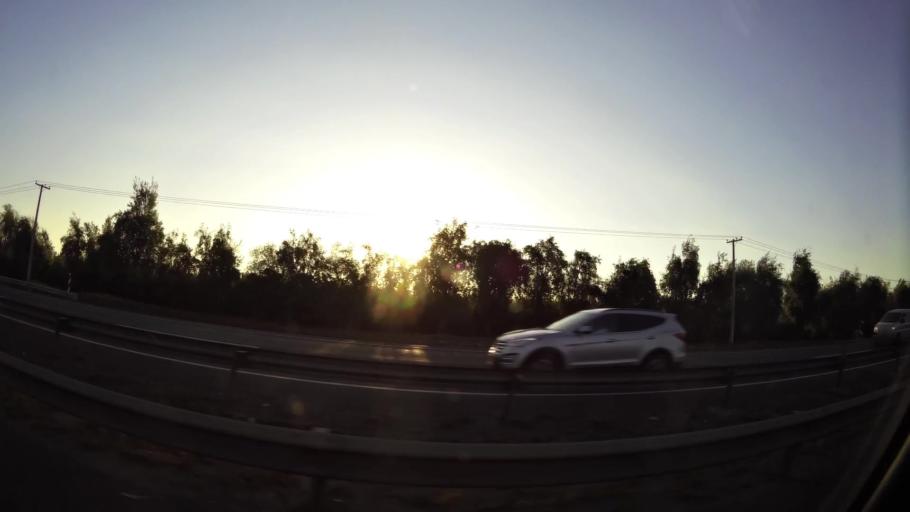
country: CL
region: Santiago Metropolitan
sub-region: Provincia de Talagante
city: Penaflor
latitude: -33.5734
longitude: -70.8495
